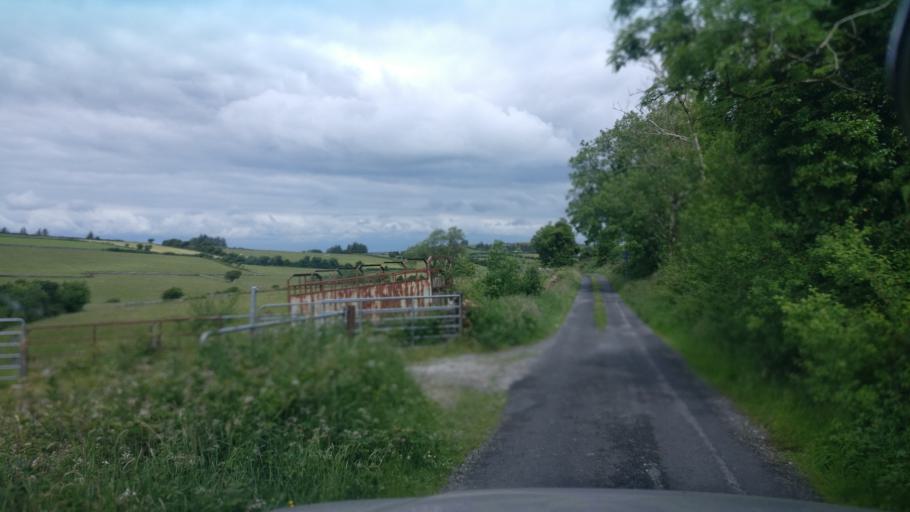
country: IE
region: Connaught
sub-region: County Galway
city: Loughrea
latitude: 53.1547
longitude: -8.5558
